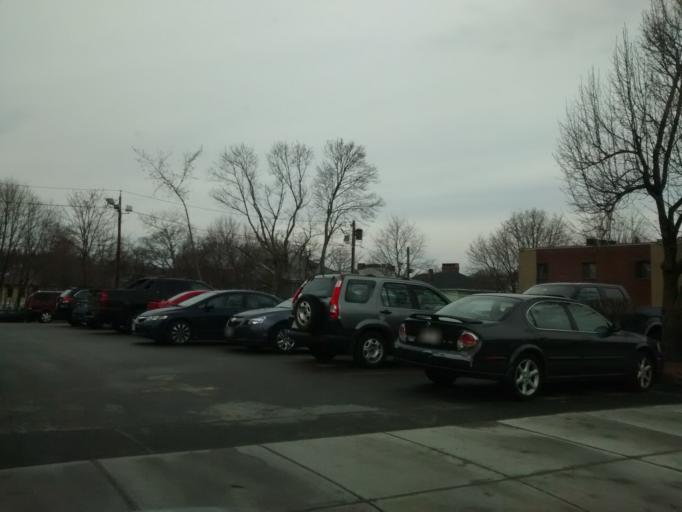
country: US
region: Massachusetts
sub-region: Worcester County
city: Worcester
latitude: 42.2821
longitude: -71.7926
